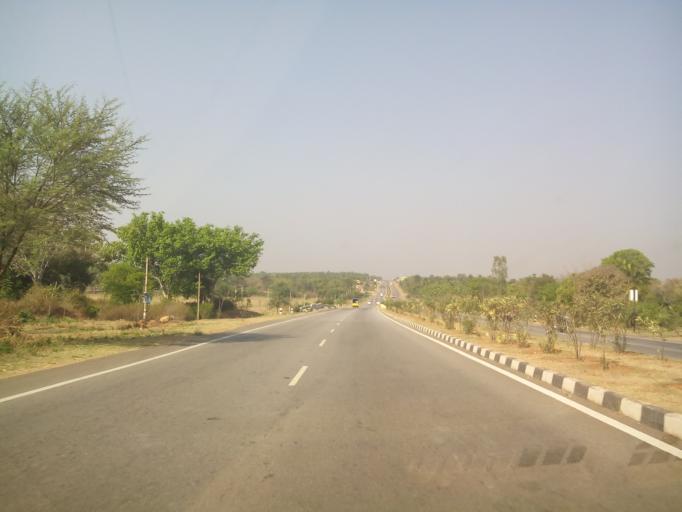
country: IN
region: Karnataka
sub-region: Tumkur
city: Kunigal
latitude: 13.0402
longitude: 77.1083
